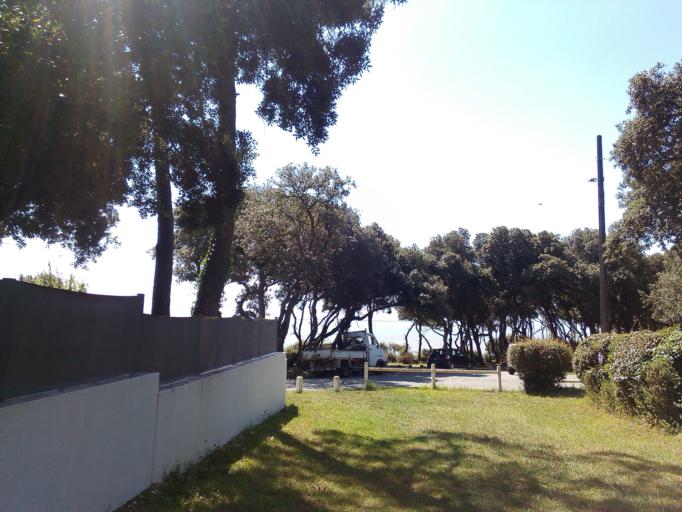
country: FR
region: Poitou-Charentes
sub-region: Departement de la Charente-Maritime
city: Saint-Palais-sur-Mer
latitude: 45.6351
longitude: -1.0723
